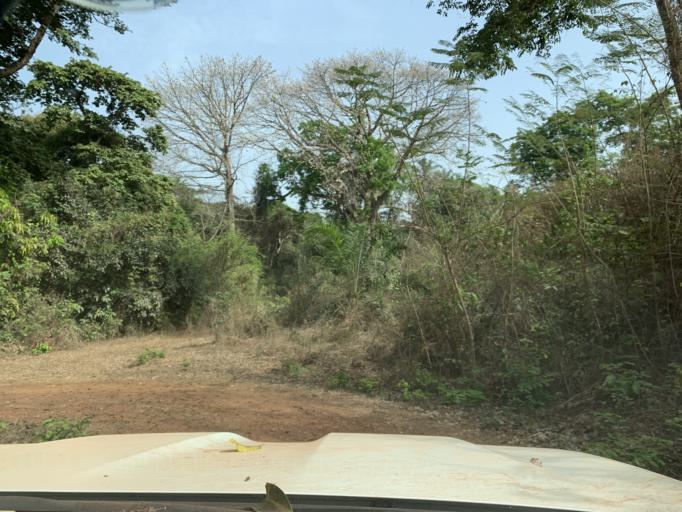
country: GN
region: Kindia
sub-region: Kindia
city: Kindia
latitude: 9.9755
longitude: -12.9836
